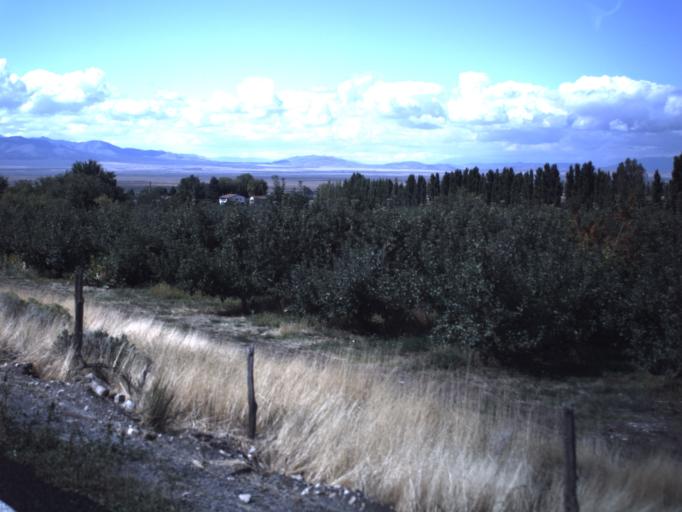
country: US
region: Utah
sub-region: Utah County
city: Genola
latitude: 40.0024
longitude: -111.8167
